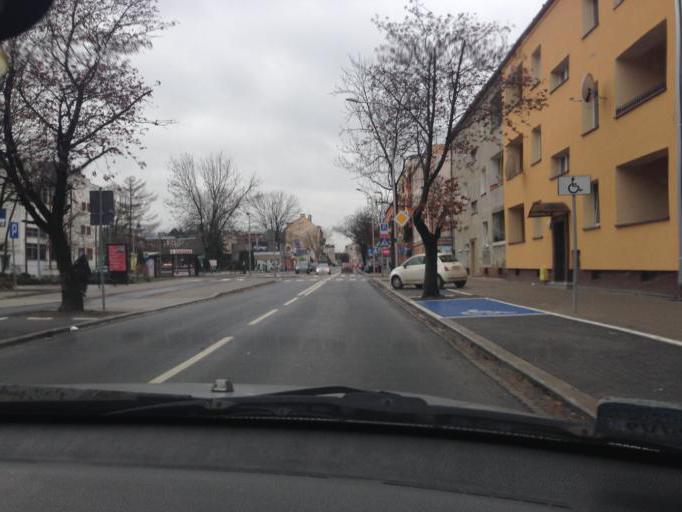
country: PL
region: Opole Voivodeship
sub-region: Powiat opolski
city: Opole
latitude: 50.6733
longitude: 17.9301
